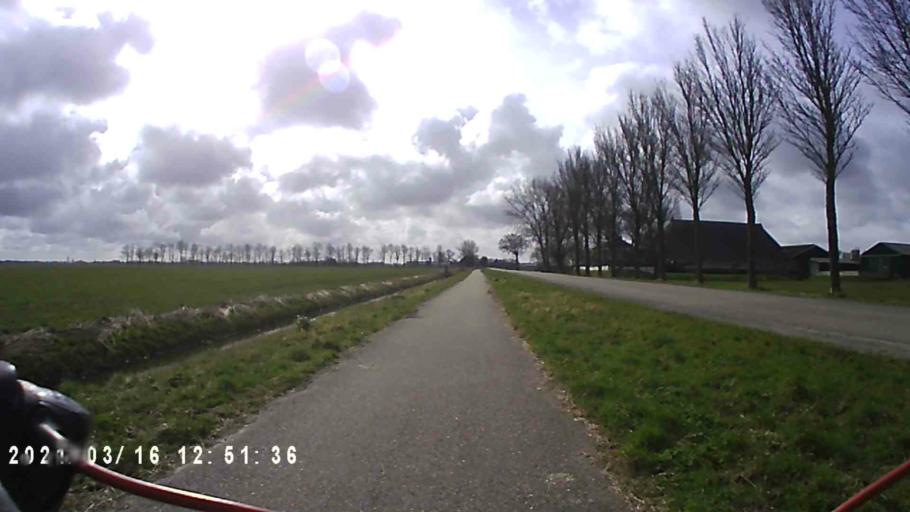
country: NL
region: Friesland
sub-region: Gemeente Het Bildt
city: Sint Annaparochie
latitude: 53.2592
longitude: 5.6797
